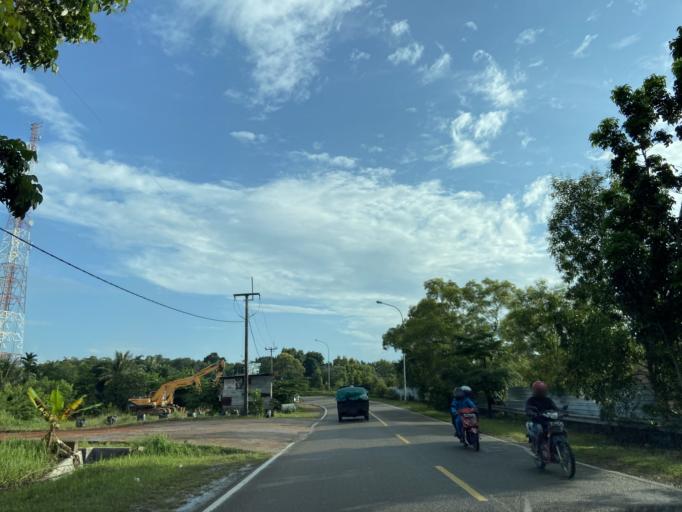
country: SG
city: Singapore
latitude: 0.9739
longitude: 104.0540
